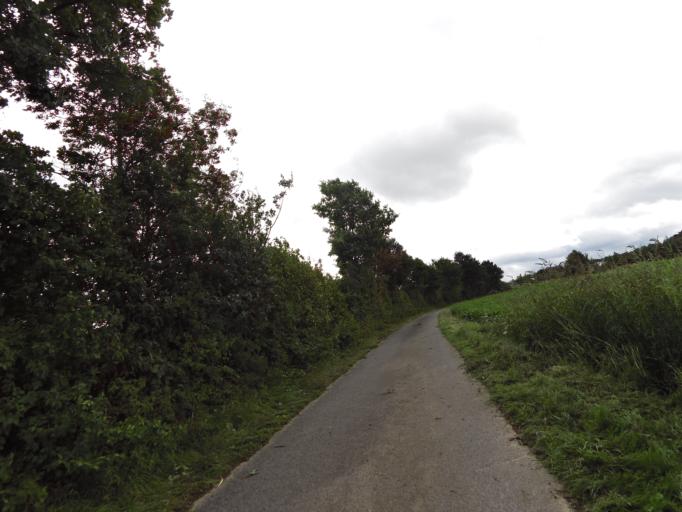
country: DE
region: Rheinland-Pfalz
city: Kalenborn
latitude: 50.5745
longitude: 7.0288
